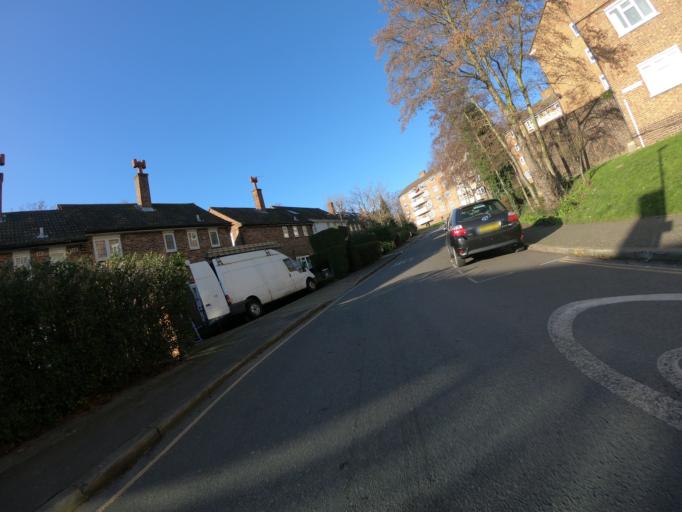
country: GB
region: England
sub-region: Greater London
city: Blackheath
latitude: 51.4665
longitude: 0.0013
